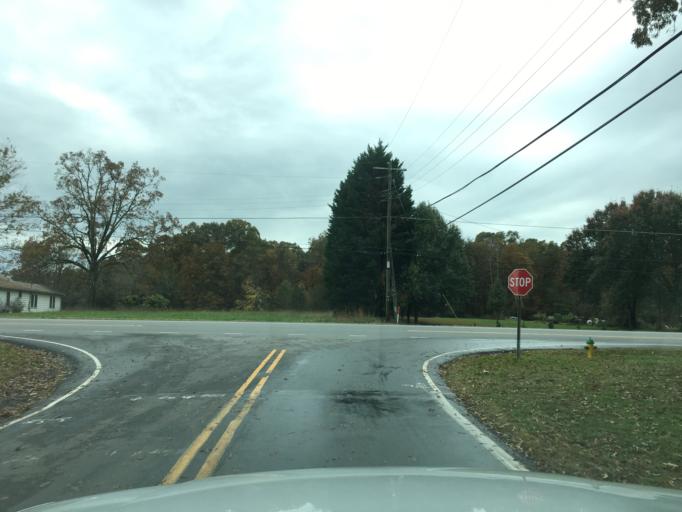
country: US
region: North Carolina
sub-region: Catawba County
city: Maiden
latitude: 35.5946
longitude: -81.2468
